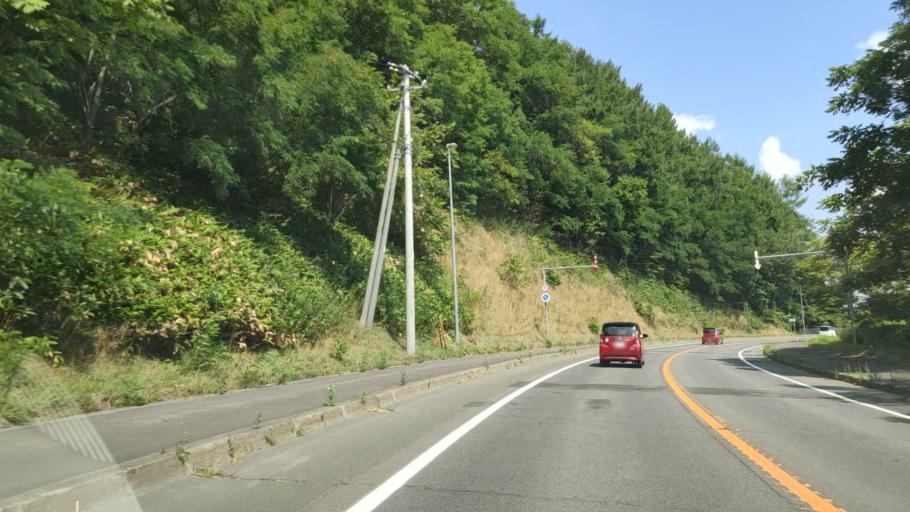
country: JP
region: Hokkaido
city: Shimo-furano
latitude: 43.4712
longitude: 142.4531
